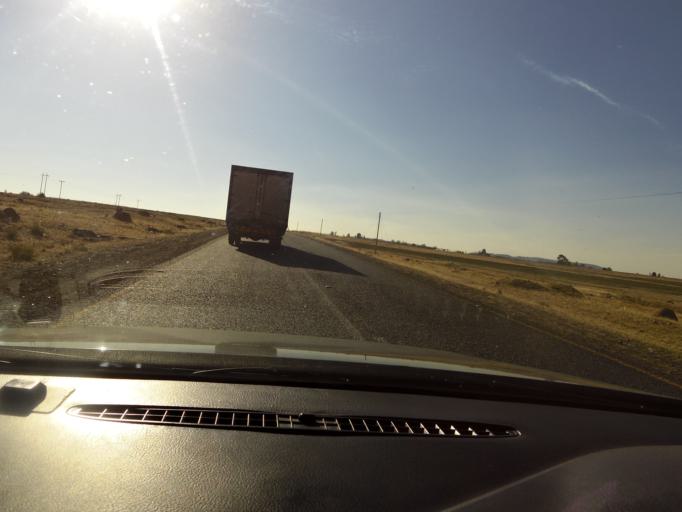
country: LS
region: Mohale's Hoek District
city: Mohale's Hoek
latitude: -30.0006
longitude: 27.3427
